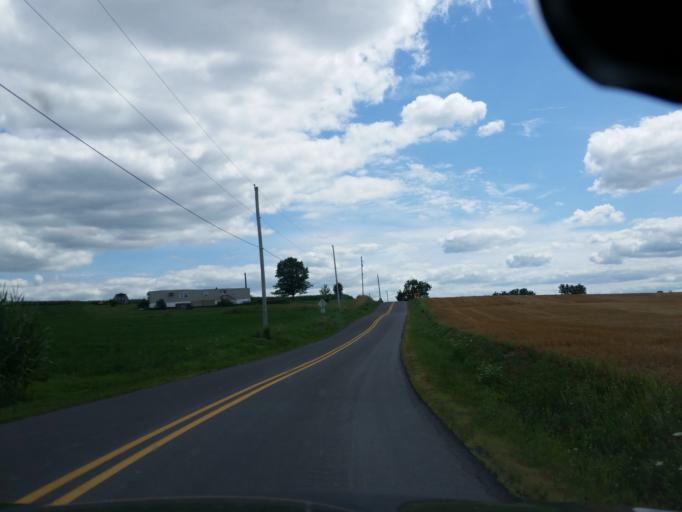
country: US
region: Pennsylvania
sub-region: Union County
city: Lewisburg
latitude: 41.0027
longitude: -76.9021
